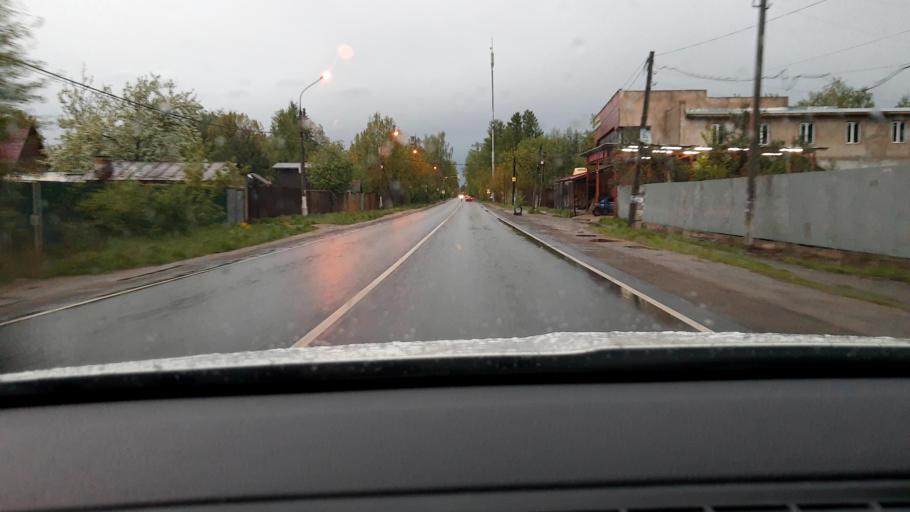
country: RU
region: Moskovskaya
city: Zagoryanskiy
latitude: 55.9176
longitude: 37.9156
